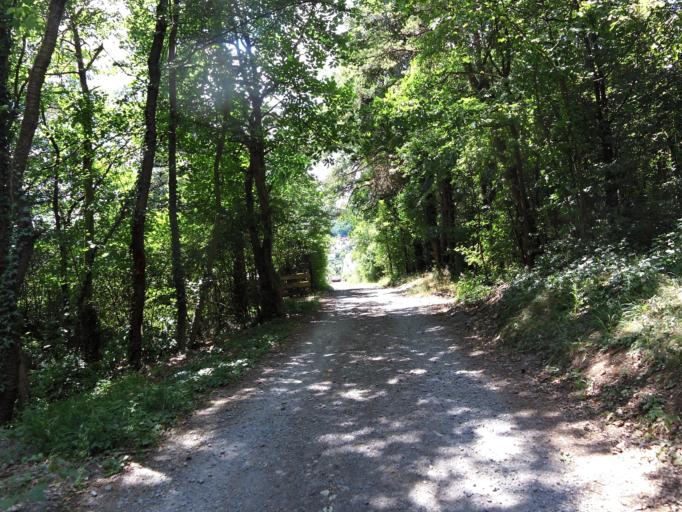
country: DE
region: Bavaria
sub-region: Regierungsbezirk Unterfranken
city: Gadheim
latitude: 49.8317
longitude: 9.9231
